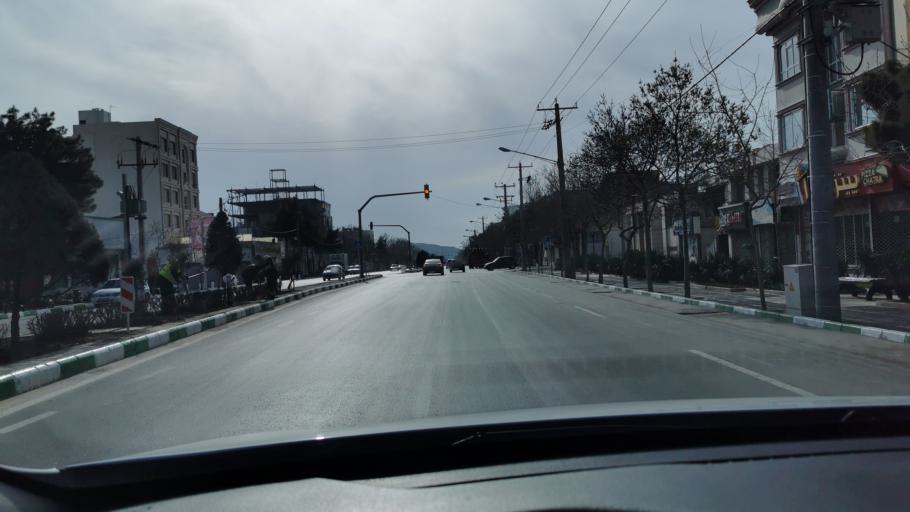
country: IR
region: Razavi Khorasan
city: Mashhad
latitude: 36.2896
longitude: 59.5401
